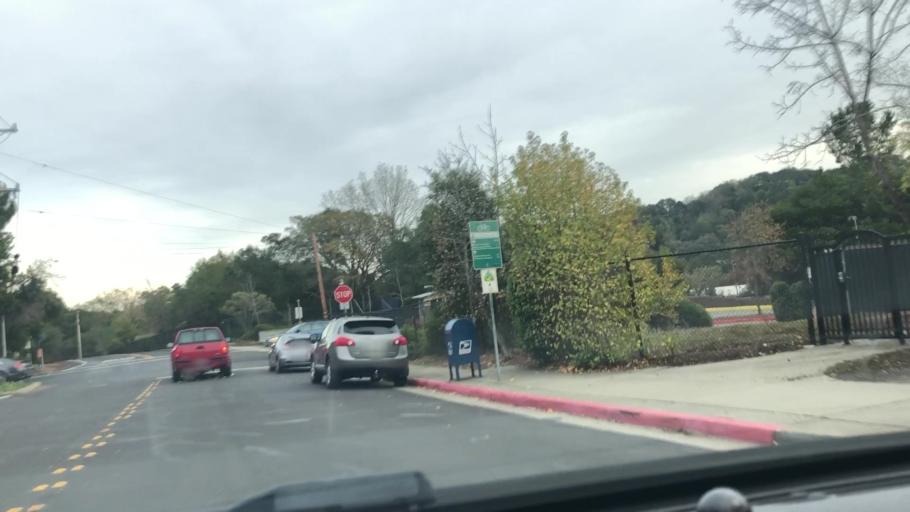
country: US
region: California
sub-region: Contra Costa County
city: Orinda
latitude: 37.8931
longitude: -122.1521
